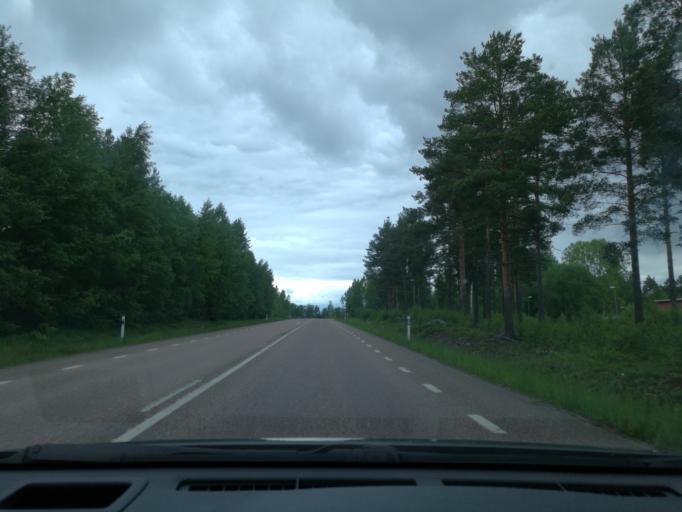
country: SE
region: Dalarna
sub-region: Smedjebackens Kommun
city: Smedjebacken
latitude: 60.1346
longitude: 15.3971
